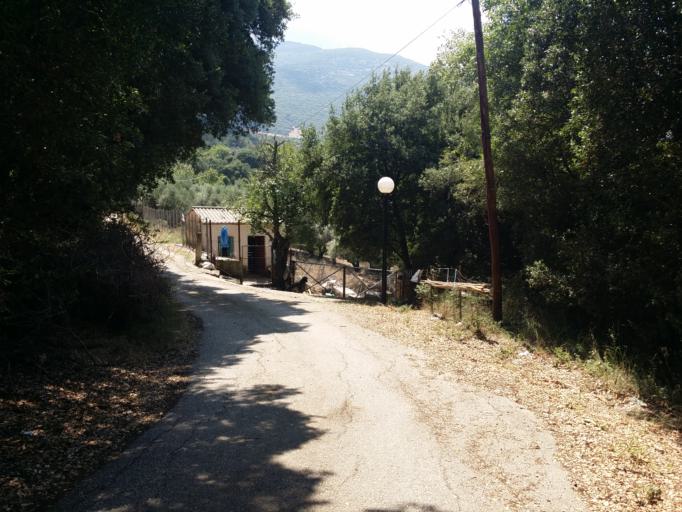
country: GR
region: West Greece
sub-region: Nomos Aitolias kai Akarnanias
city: Monastirakion
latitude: 38.8616
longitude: 20.9545
